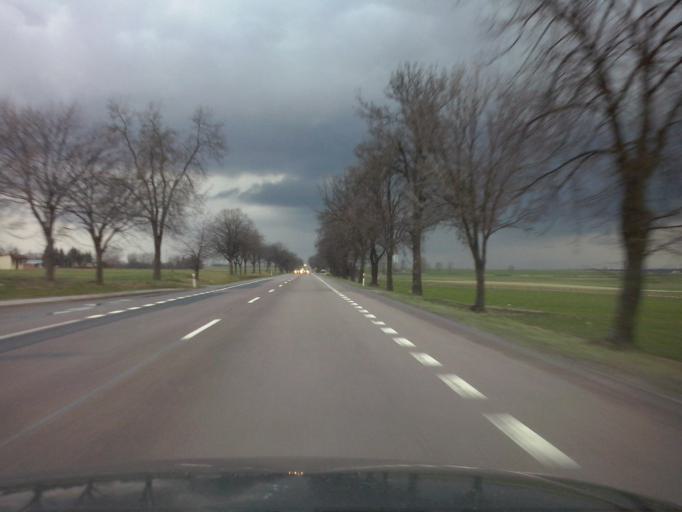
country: PL
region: Lublin Voivodeship
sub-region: Powiat chelmski
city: Rejowiec Fabryczny
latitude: 51.1769
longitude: 23.2310
